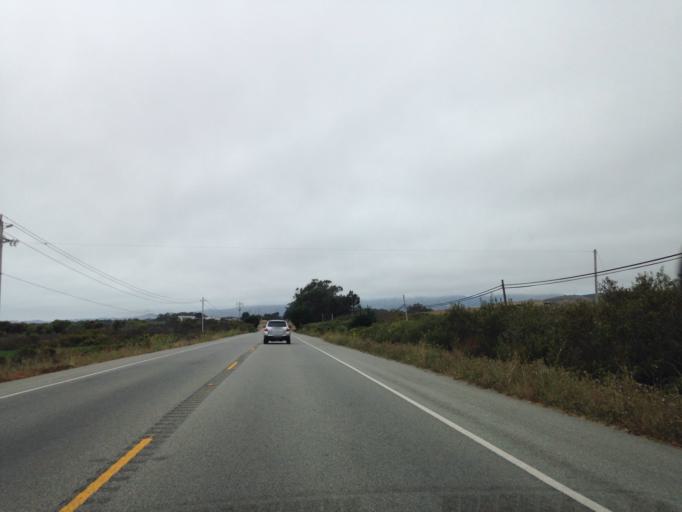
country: US
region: California
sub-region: San Mateo County
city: Half Moon Bay
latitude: 37.4150
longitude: -122.4237
